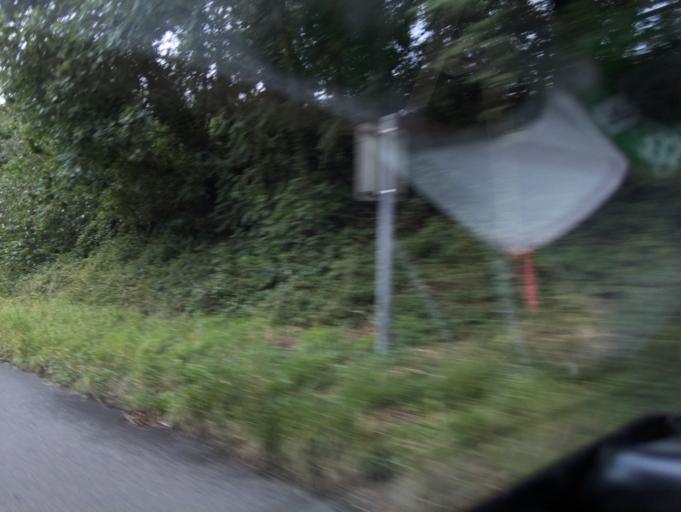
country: GB
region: England
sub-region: Devon
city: Kingsbridge
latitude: 50.2900
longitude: -3.7819
